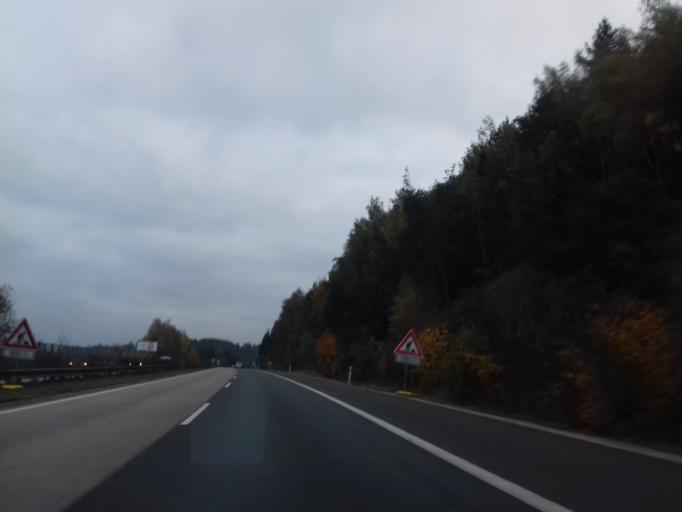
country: CZ
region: Central Bohemia
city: Ondrejov
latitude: 49.8704
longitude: 14.7722
